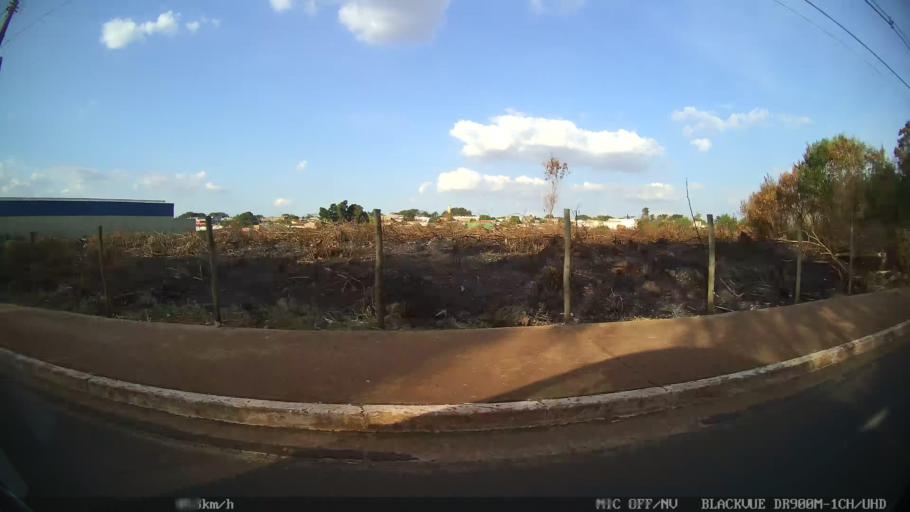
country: BR
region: Sao Paulo
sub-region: Ribeirao Preto
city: Ribeirao Preto
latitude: -21.1399
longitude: -47.8030
